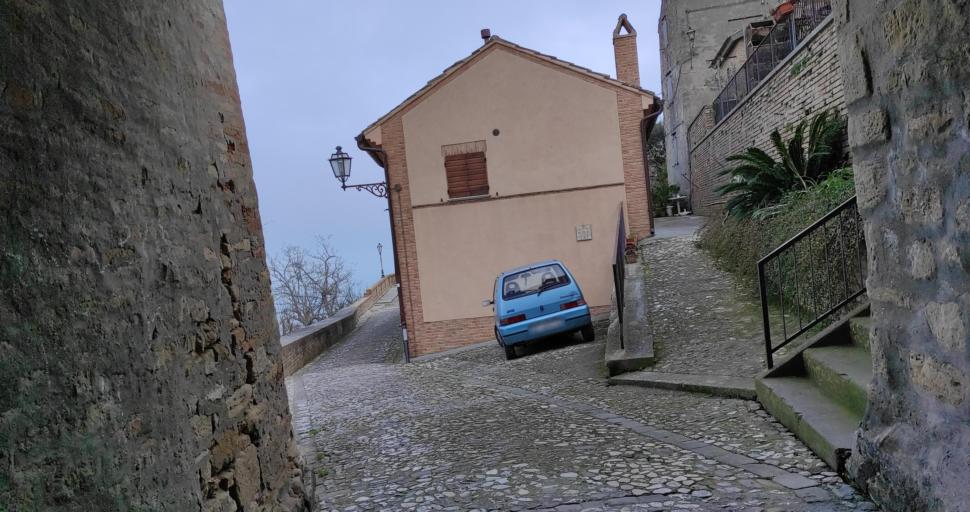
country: IT
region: The Marches
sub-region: Province of Fermo
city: Altidona
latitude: 43.1416
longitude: 13.8101
